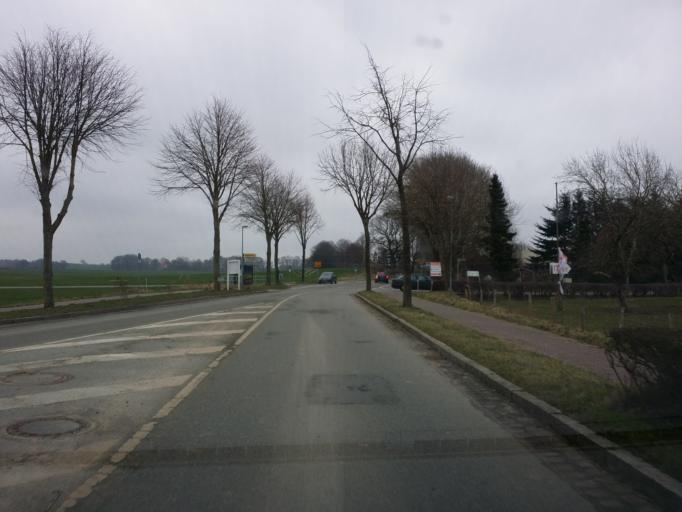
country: DE
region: Schleswig-Holstein
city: Bredenbek
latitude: 54.3242
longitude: 9.8767
